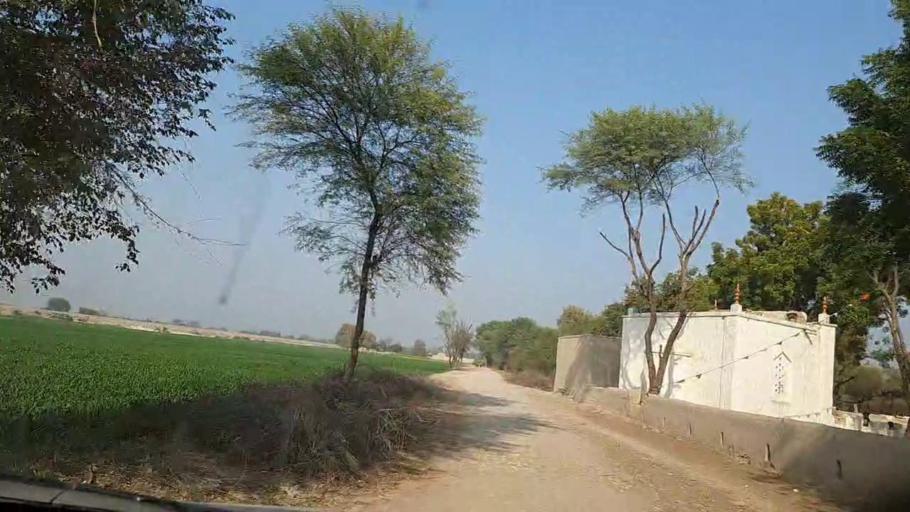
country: PK
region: Sindh
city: Moro
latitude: 26.7970
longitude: 67.9439
